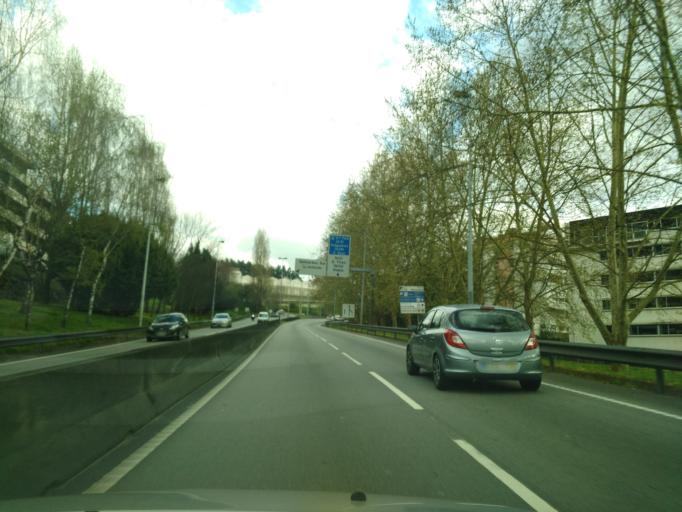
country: PT
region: Braga
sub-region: Guimaraes
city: Urgeses
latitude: 41.4359
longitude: -8.3039
